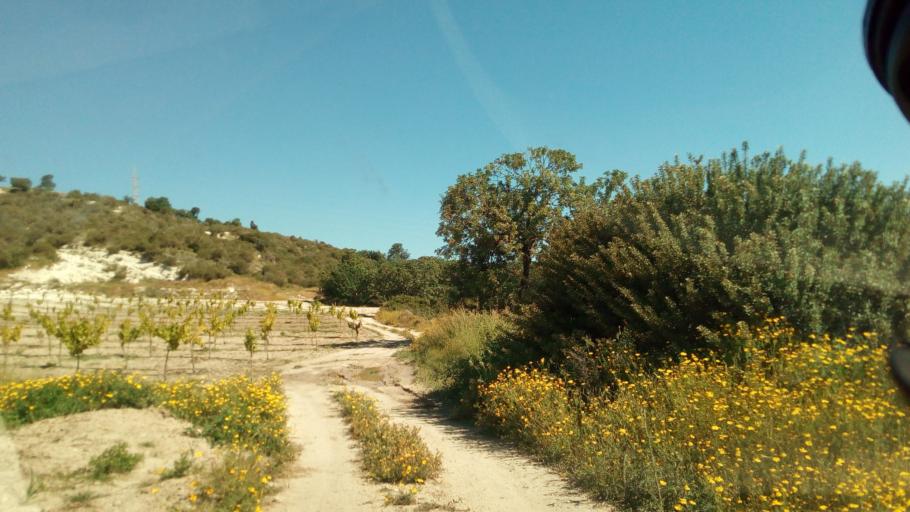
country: CY
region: Limassol
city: Pissouri
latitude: 34.6752
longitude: 32.6884
